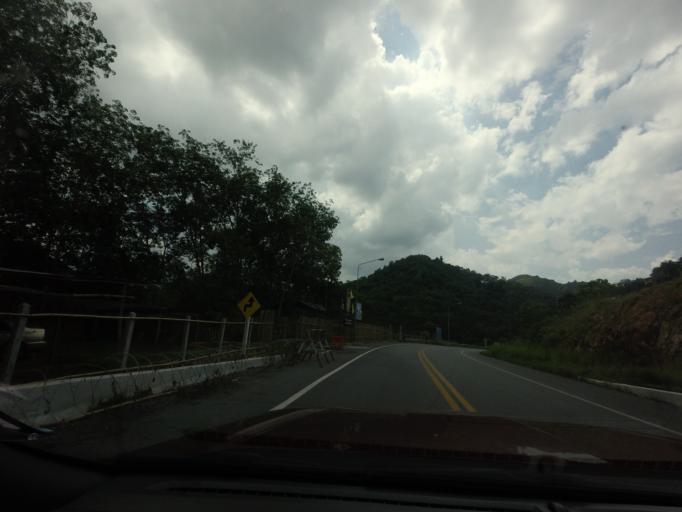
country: TH
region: Yala
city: Than To
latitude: 6.0495
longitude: 101.1971
